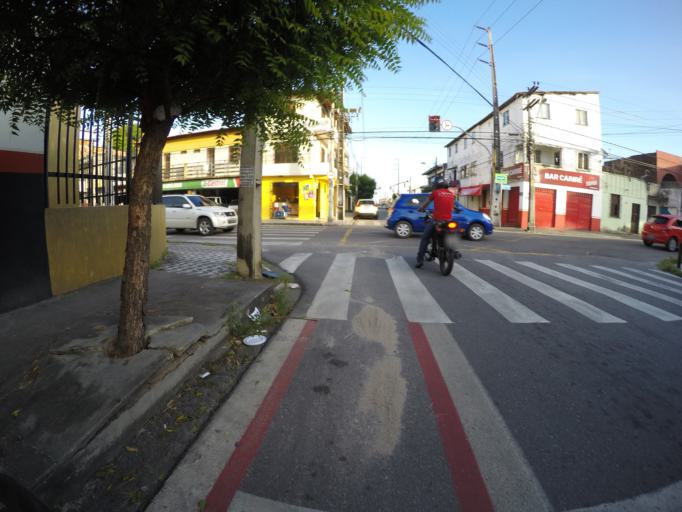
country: BR
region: Ceara
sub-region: Fortaleza
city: Fortaleza
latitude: -3.7559
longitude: -38.5132
